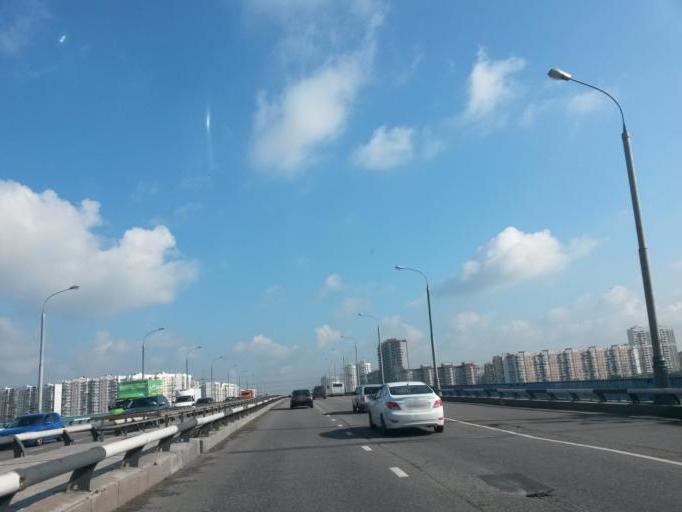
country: RU
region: Moscow
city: Brateyevo
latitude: 55.6388
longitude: 37.7483
